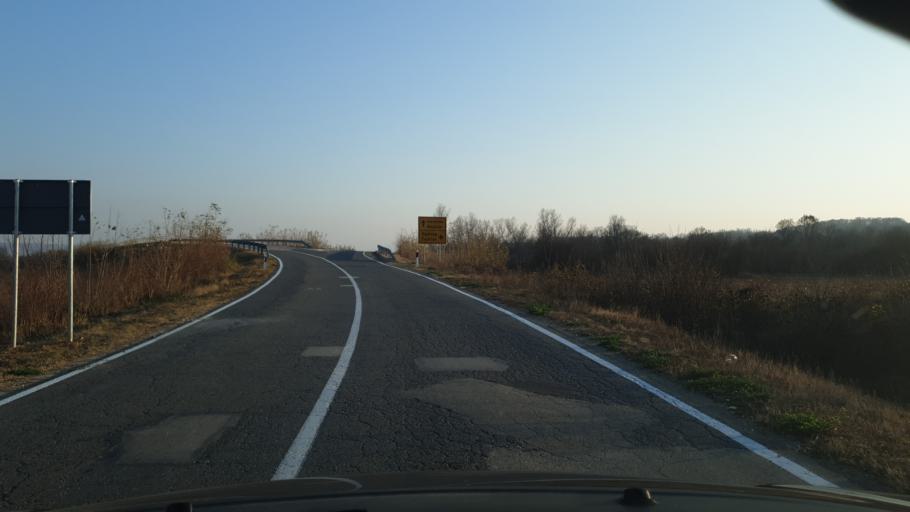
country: RS
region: Central Serbia
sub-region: Zajecarski Okrug
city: Zajecar
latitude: 43.9793
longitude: 22.2905
